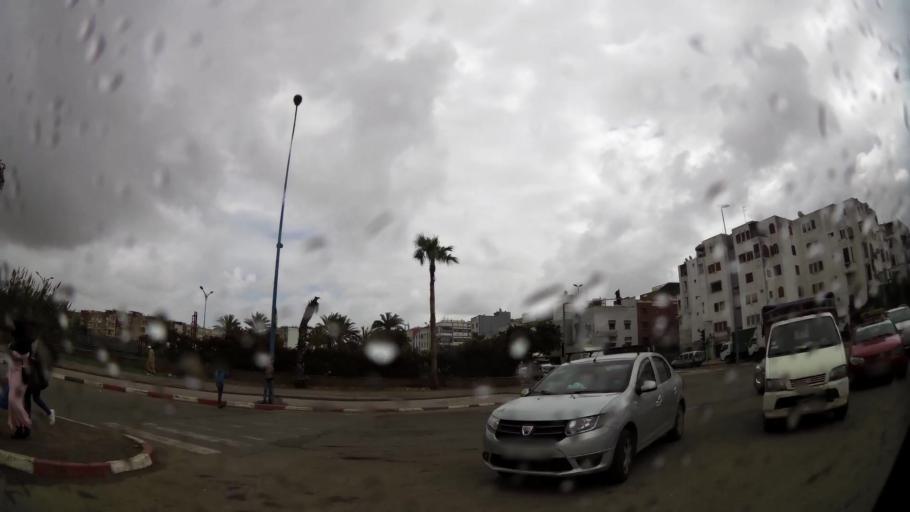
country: MA
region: Grand Casablanca
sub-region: Mediouna
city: Tit Mellil
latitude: 33.6159
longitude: -7.4999
